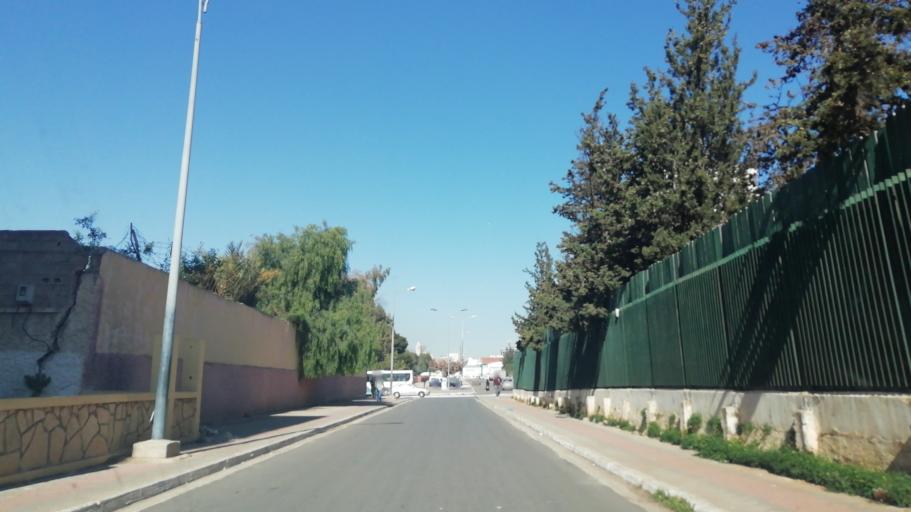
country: DZ
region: Oran
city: Oran
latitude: 35.6803
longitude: -0.6394
